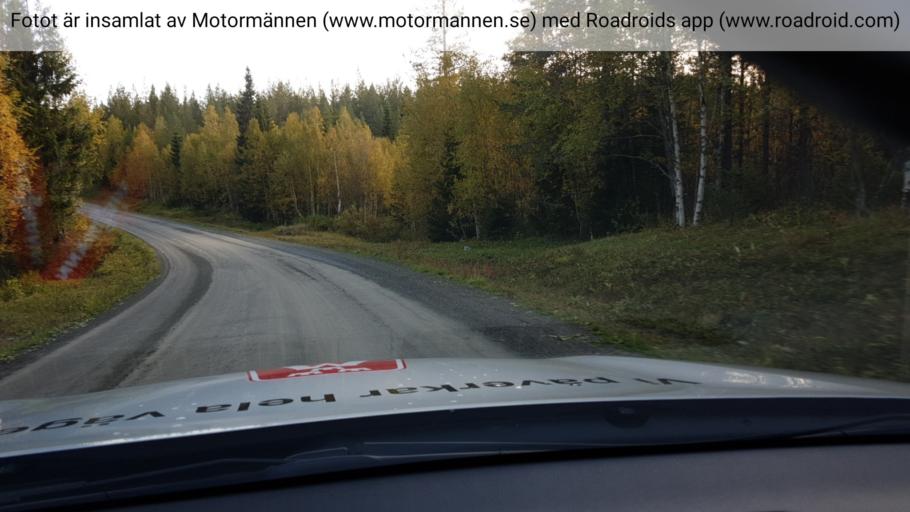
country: SE
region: Jaemtland
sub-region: Krokoms Kommun
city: Krokom
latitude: 63.7443
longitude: 14.4671
